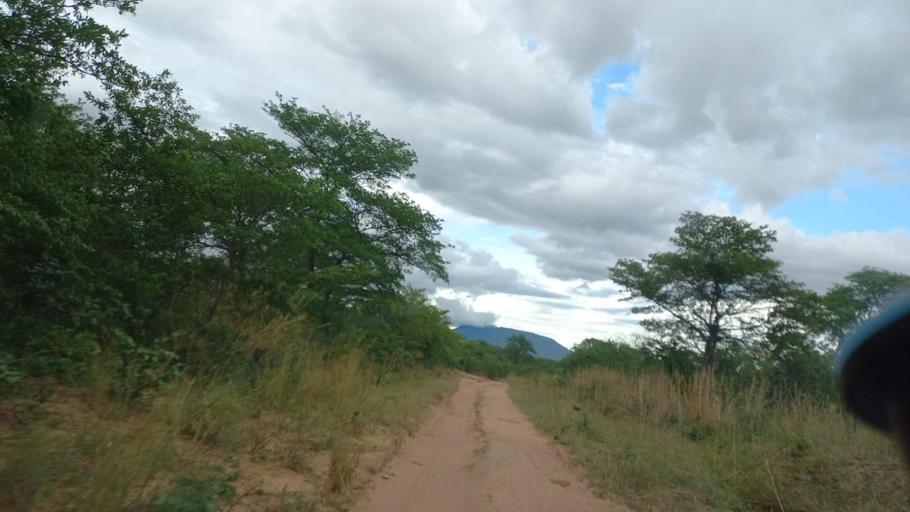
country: ZM
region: Lusaka
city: Luangwa
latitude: -15.5631
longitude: 30.3304
